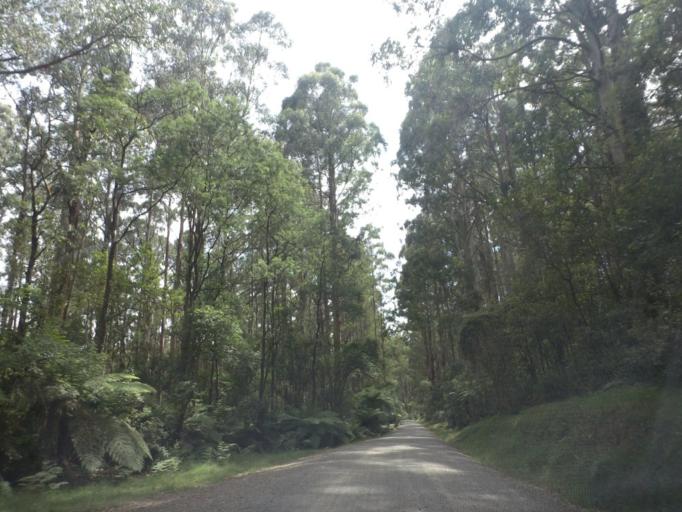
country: AU
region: Victoria
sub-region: Yarra Ranges
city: Healesville
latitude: -37.5321
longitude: 145.5156
